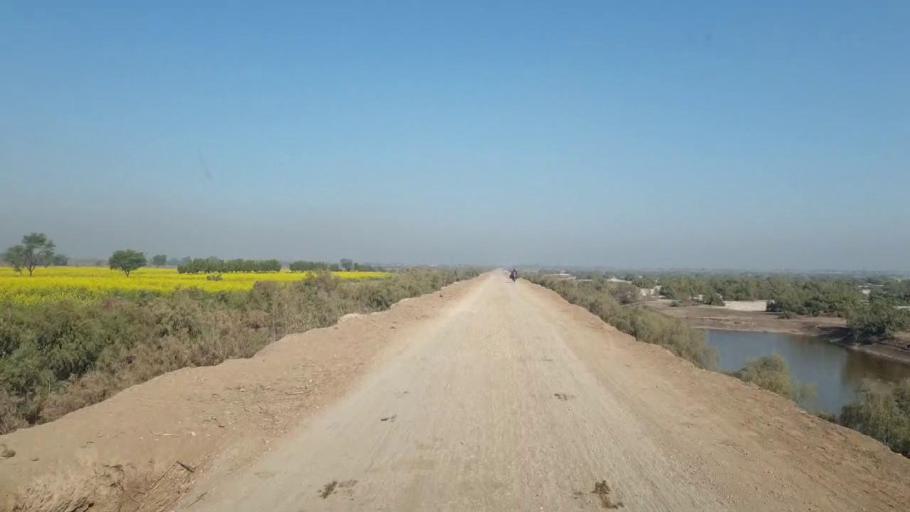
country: PK
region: Sindh
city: Shahdadpur
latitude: 25.9777
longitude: 68.4970
